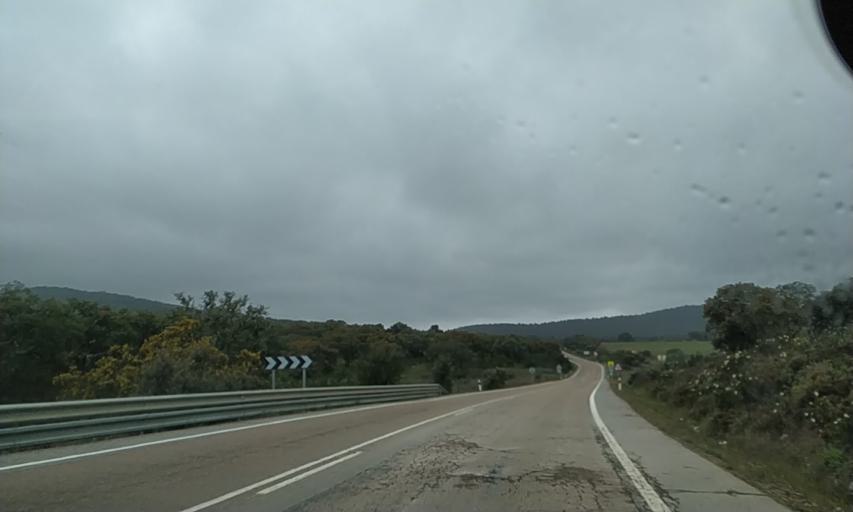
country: ES
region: Extremadura
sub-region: Provincia de Caceres
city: Malpartida de Caceres
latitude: 39.3008
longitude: -6.5162
